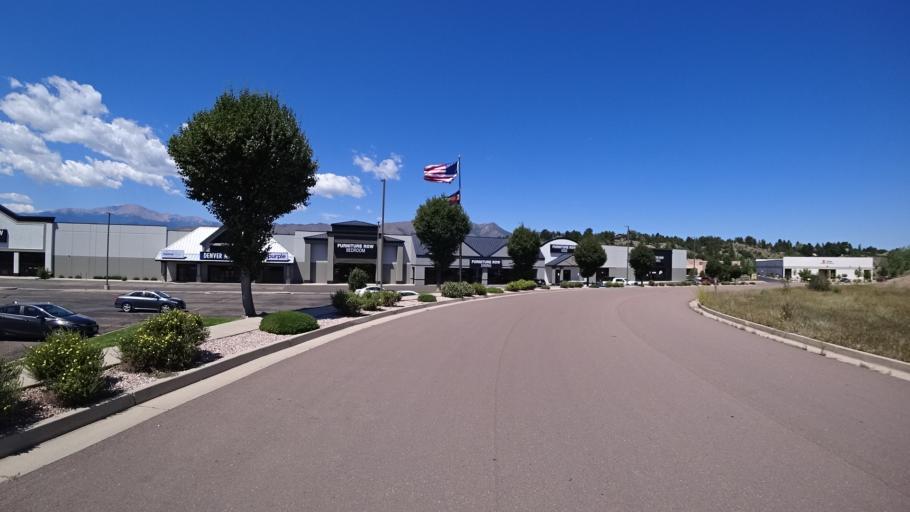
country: US
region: Colorado
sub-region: El Paso County
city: Air Force Academy
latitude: 38.9221
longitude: -104.8167
